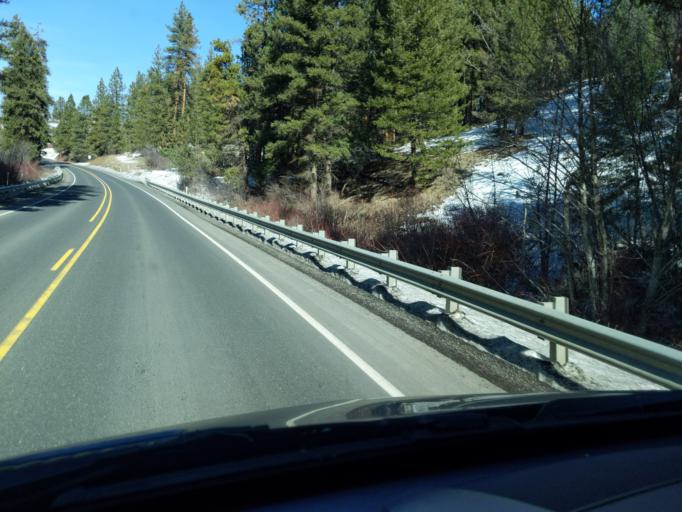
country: US
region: Oregon
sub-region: Grant County
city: John Day
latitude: 44.8759
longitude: -119.0172
